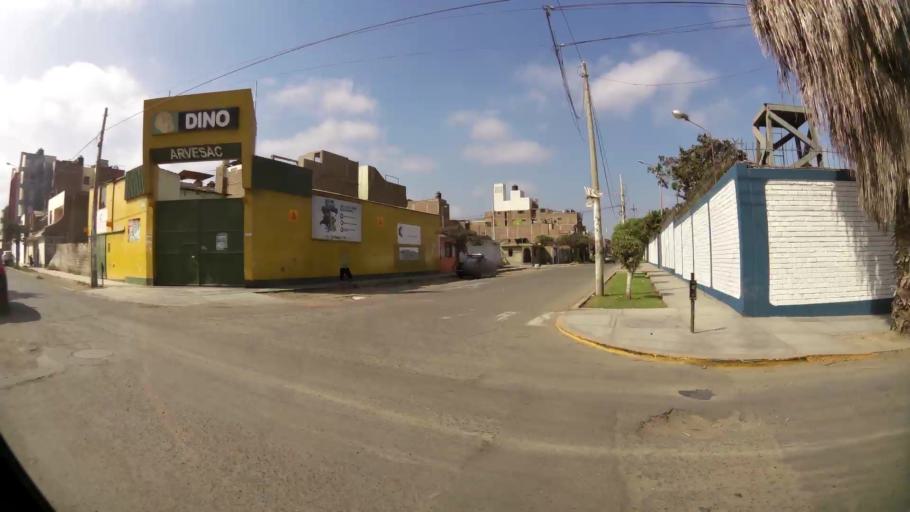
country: PE
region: La Libertad
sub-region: Provincia de Trujillo
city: Trujillo
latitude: -8.1244
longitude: -79.0178
